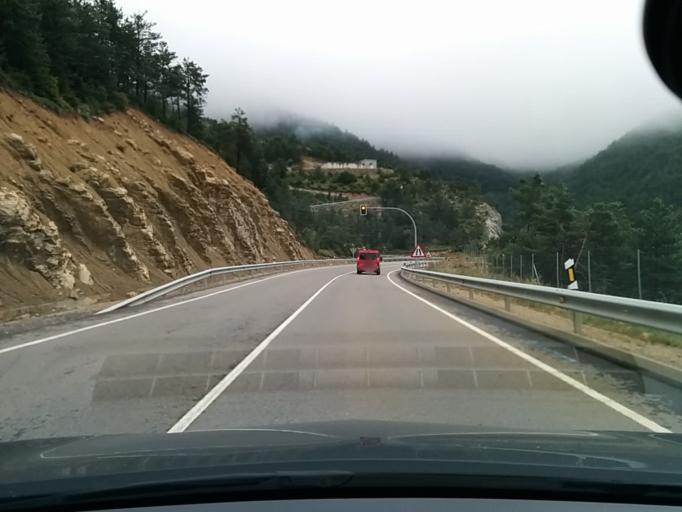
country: ES
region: Aragon
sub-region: Provincia de Huesca
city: Fiscal
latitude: 42.4679
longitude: -0.1941
